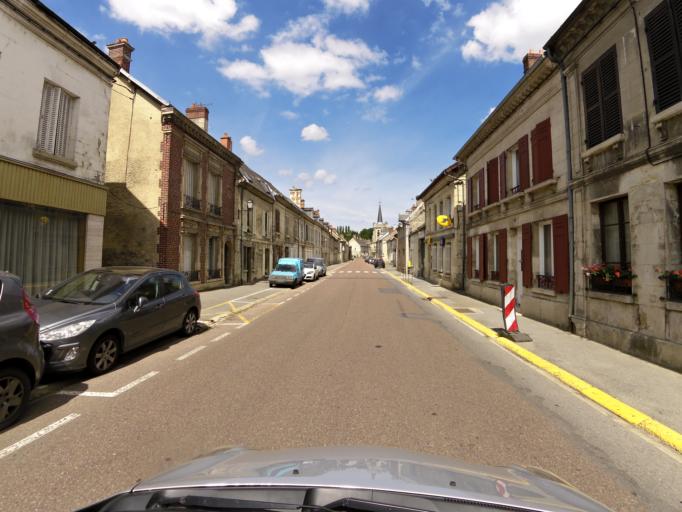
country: FR
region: Picardie
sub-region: Departement de l'Aisne
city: La Ferte-Milon
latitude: 49.1782
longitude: 3.1251
